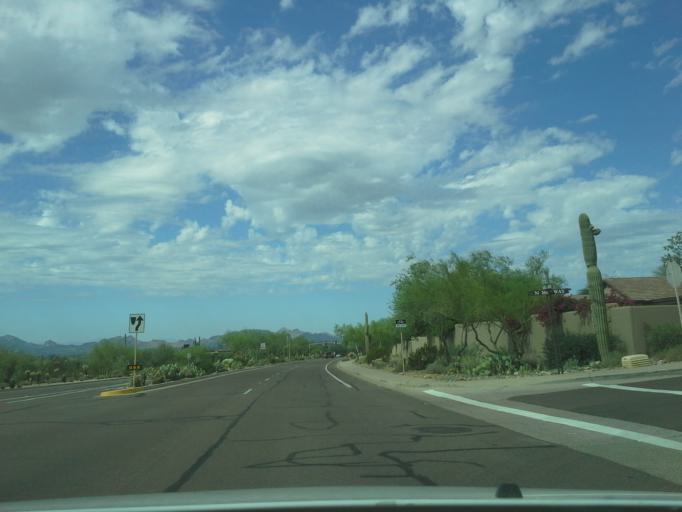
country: US
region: Arizona
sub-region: Maricopa County
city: Scottsdale
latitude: 33.6296
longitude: -111.8518
